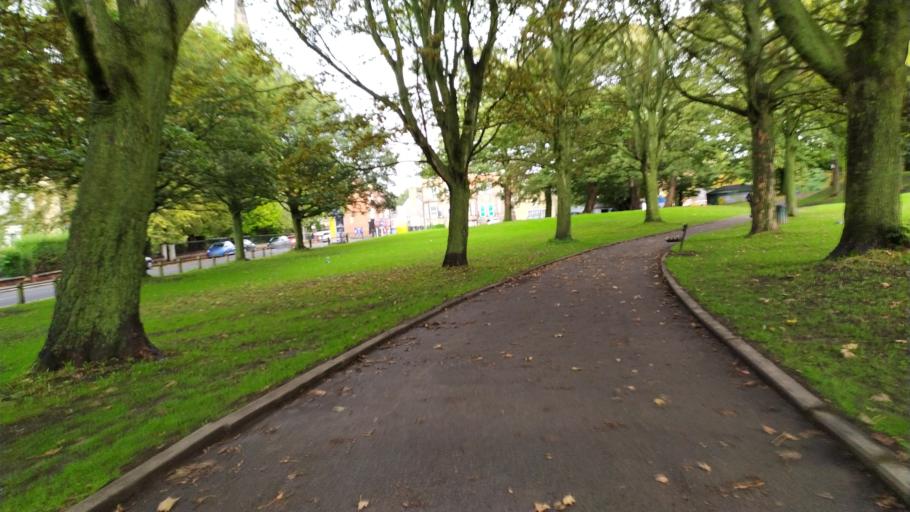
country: GB
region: England
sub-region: City and Borough of Leeds
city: Leeds
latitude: 53.8133
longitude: -1.5627
